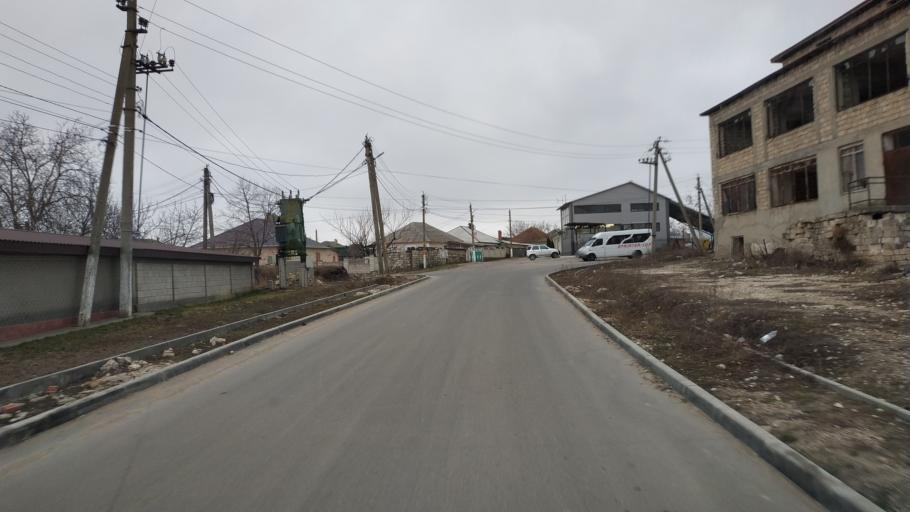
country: MD
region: Laloveni
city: Ialoveni
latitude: 46.9052
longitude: 28.7979
